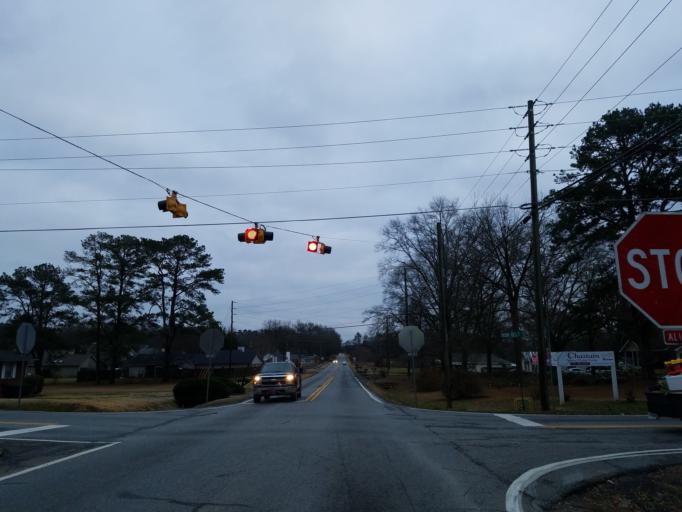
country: US
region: Georgia
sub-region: Bartow County
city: Cartersville
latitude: 34.2024
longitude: -84.8286
